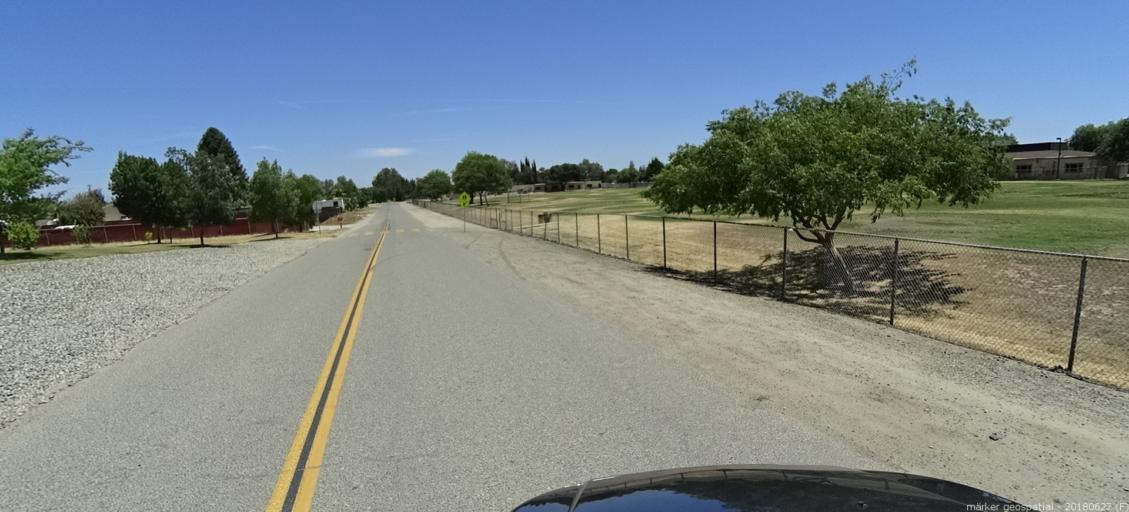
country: US
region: California
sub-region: Madera County
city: Bonadelle Ranchos-Madera Ranchos
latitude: 36.9313
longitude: -119.8879
